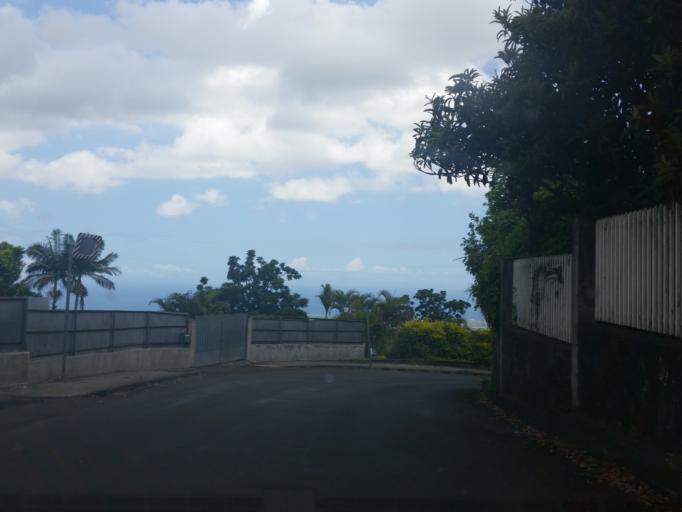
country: RE
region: Reunion
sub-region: Reunion
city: Le Tampon
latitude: -21.2545
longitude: 55.4970
